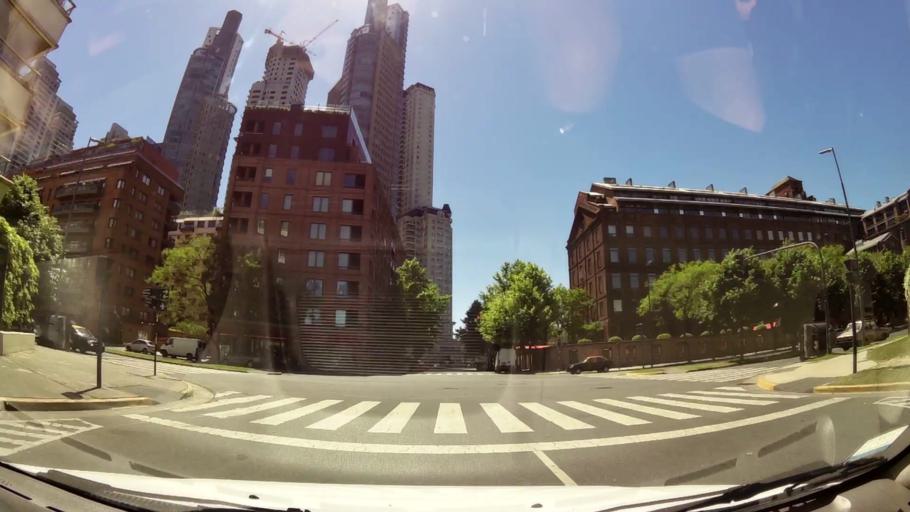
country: AR
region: Buenos Aires F.D.
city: Buenos Aires
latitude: -34.6135
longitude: -58.3626
